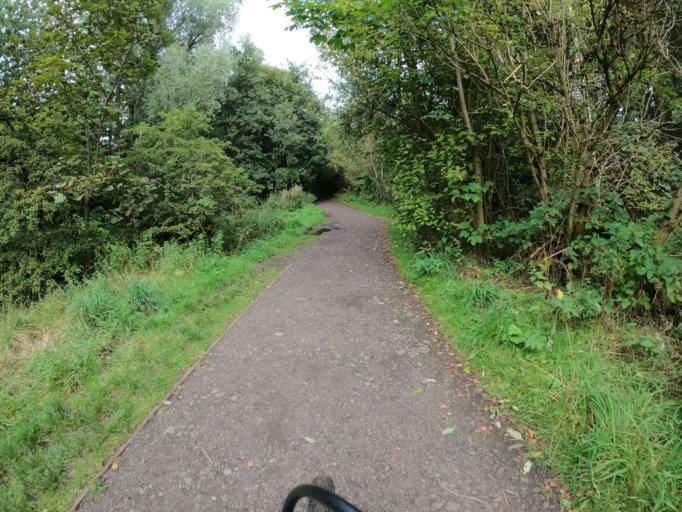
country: GB
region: Scotland
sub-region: West Lothian
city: Mid Calder
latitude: 55.8638
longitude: -3.5074
